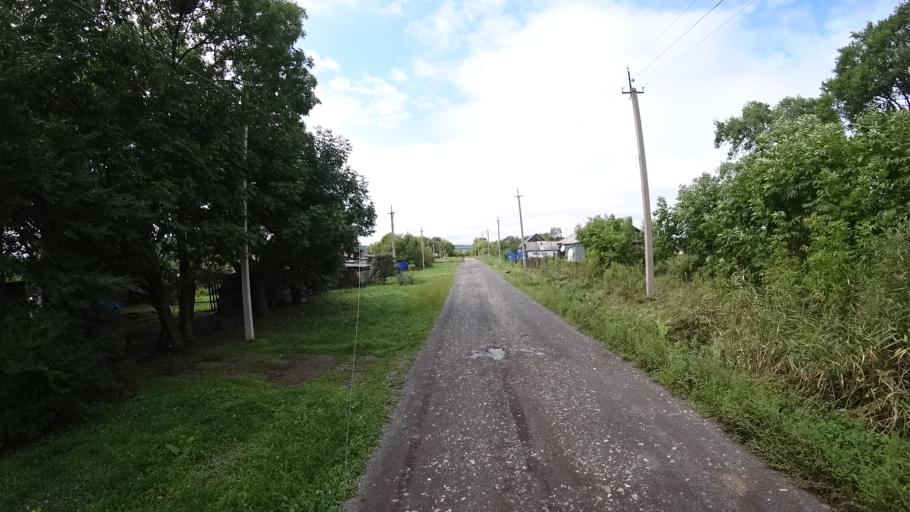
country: RU
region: Primorskiy
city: Lyalichi
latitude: 44.1397
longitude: 132.3784
